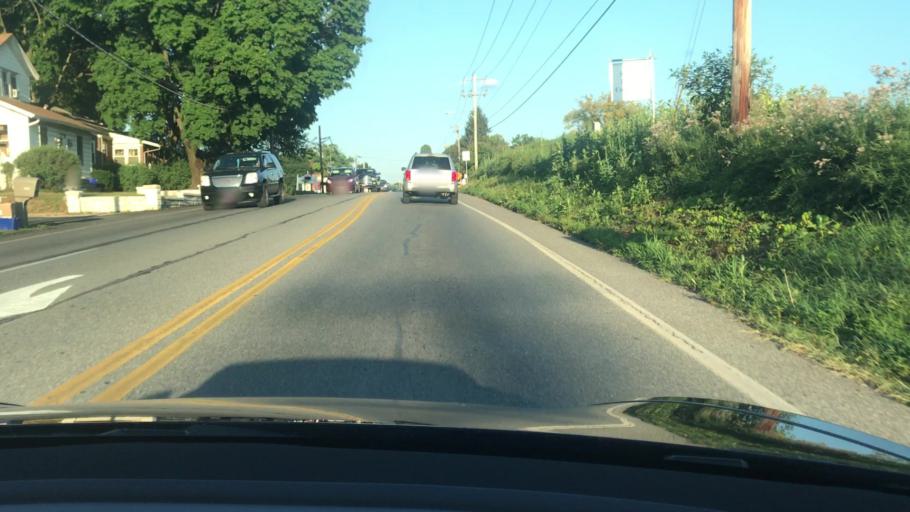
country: US
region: Pennsylvania
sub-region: York County
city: Shiloh
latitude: 39.9795
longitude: -76.8022
